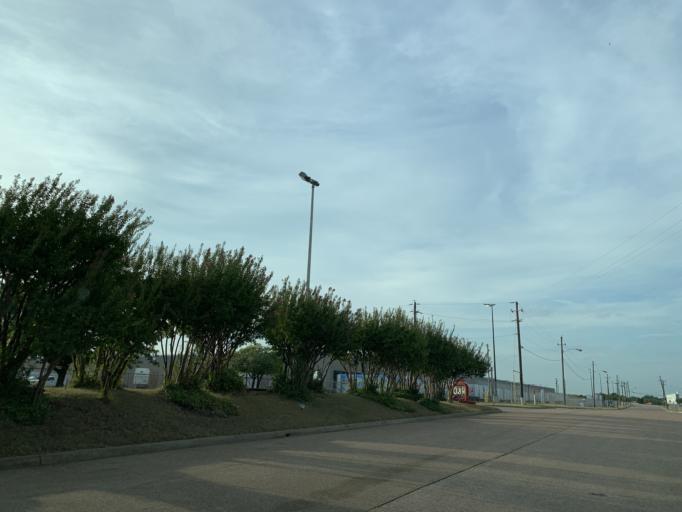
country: US
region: Texas
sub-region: Dallas County
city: Cockrell Hill
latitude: 32.6996
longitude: -96.9016
